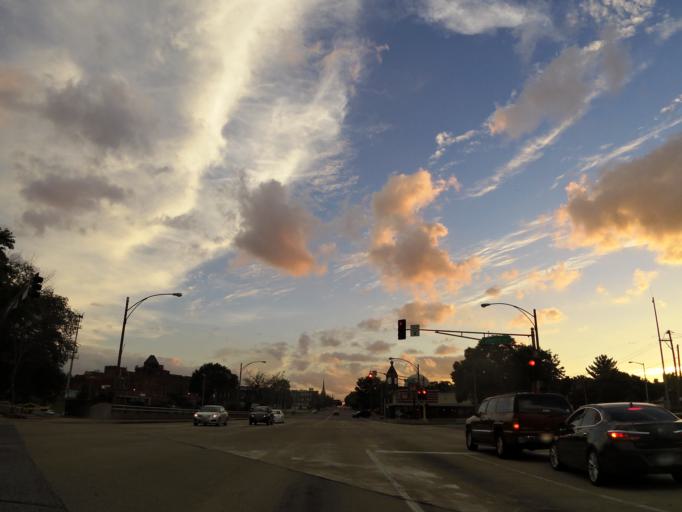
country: US
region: Missouri
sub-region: City of Saint Louis
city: St. Louis
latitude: 38.6086
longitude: -90.2121
